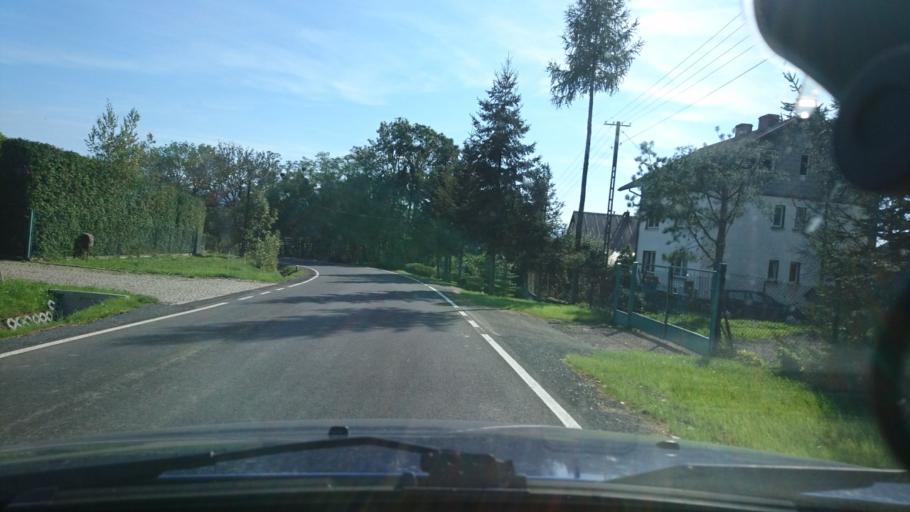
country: PL
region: Silesian Voivodeship
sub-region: Powiat cieszynski
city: Pogorze
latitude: 49.8175
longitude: 18.8575
